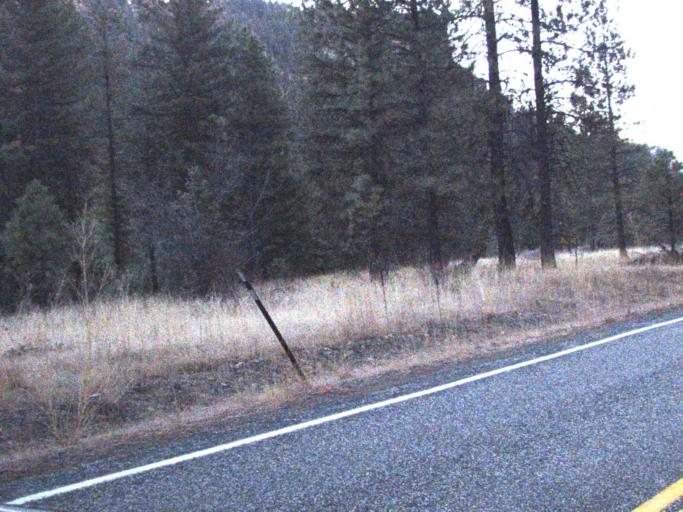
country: US
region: Washington
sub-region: Ferry County
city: Republic
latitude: 48.3783
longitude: -118.7483
